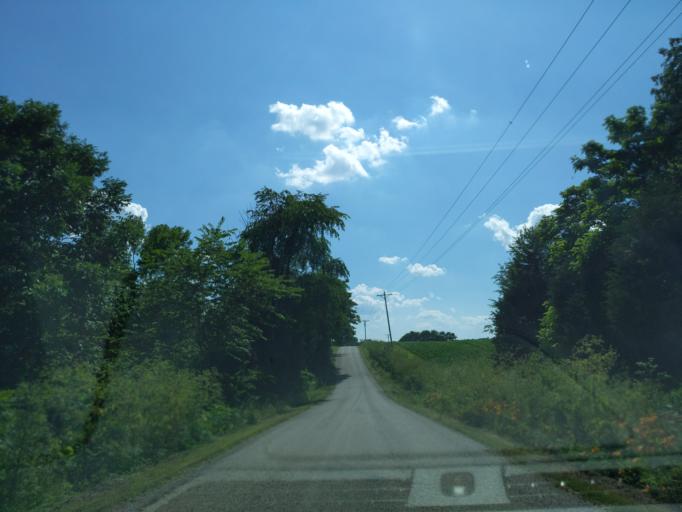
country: US
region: Indiana
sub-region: Ripley County
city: Osgood
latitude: 39.1941
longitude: -85.3904
